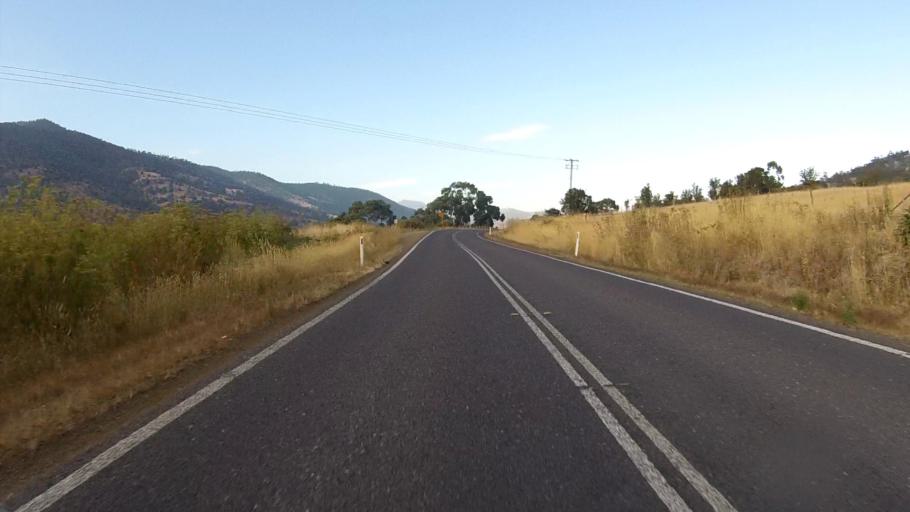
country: AU
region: Tasmania
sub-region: Glenorchy
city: Granton
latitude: -42.7498
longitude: 147.1526
